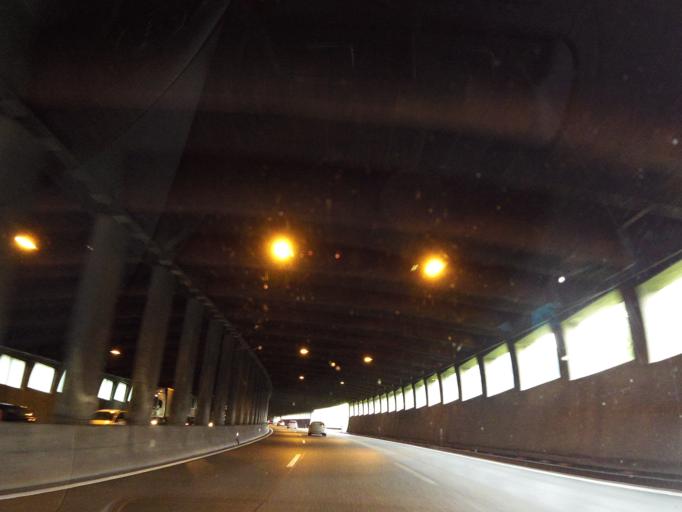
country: AT
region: Tyrol
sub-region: Politischer Bezirk Innsbruck Land
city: Patsch
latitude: 47.1920
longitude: 11.3984
